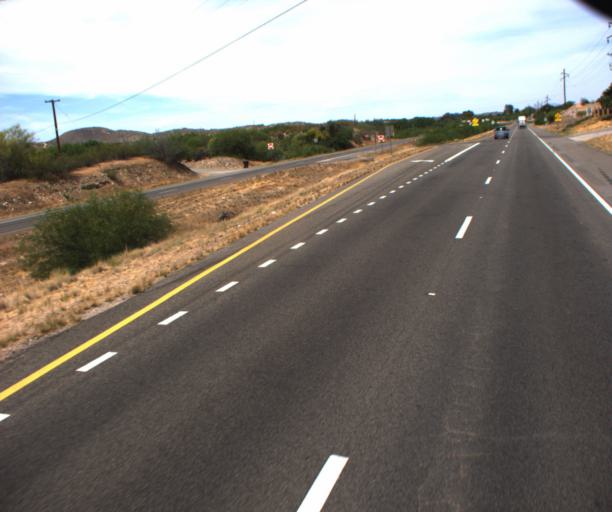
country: US
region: Arizona
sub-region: Maricopa County
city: Wickenburg
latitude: 33.9416
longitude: -112.6981
